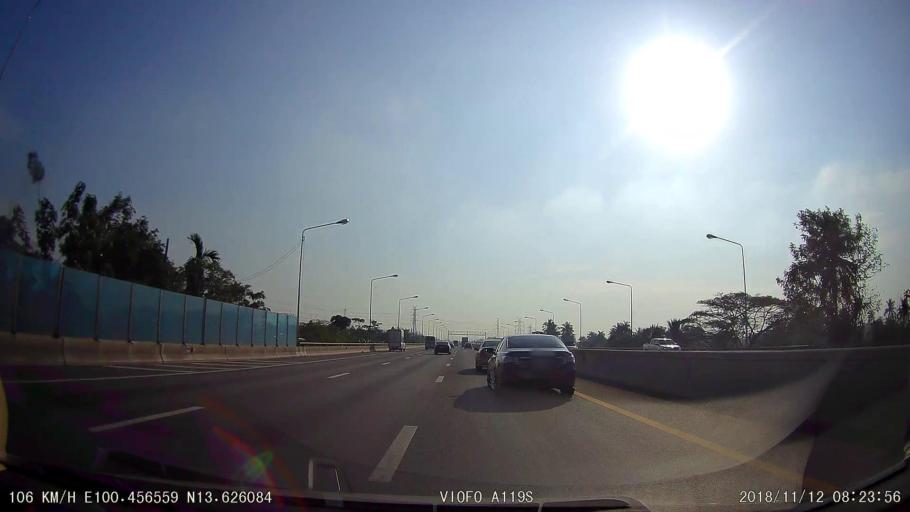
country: TH
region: Bangkok
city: Bang Khun Thian
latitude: 13.6262
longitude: 100.4571
